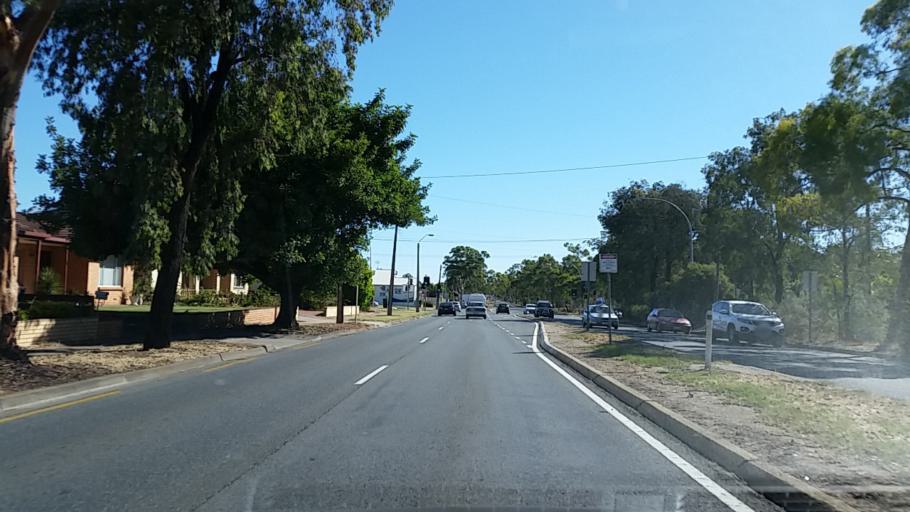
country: AU
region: South Australia
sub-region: Salisbury
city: Ingle Farm
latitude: -34.8059
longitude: 138.6500
